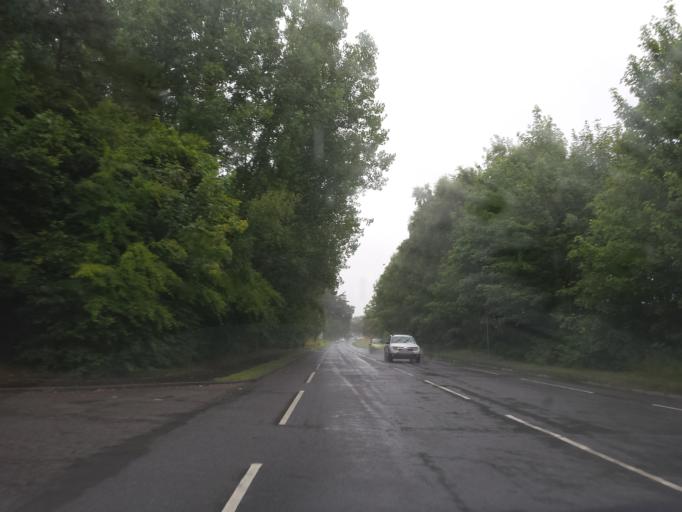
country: GB
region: England
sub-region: Warwickshire
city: Warwick
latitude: 52.3092
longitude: -1.5753
